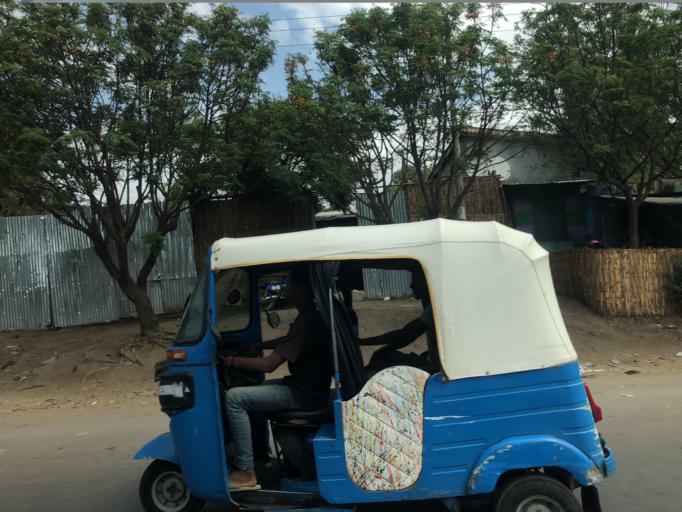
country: ET
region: Oromiya
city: Shashemene
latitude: 7.3628
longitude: 38.6711
